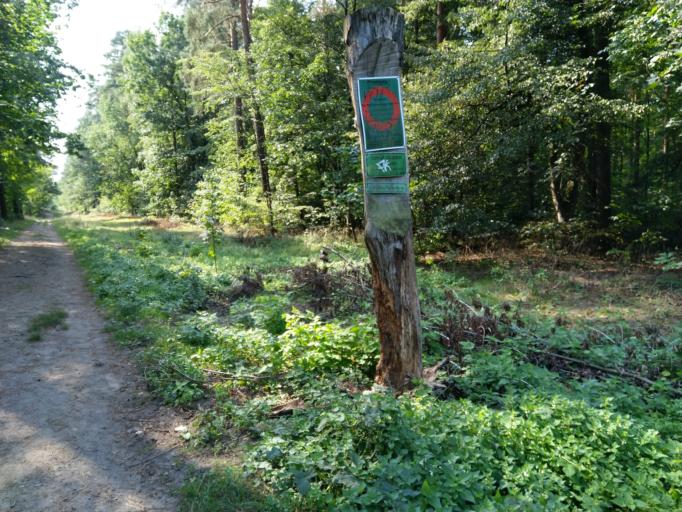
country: DE
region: Brandenburg
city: Woltersdorf
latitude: 52.4506
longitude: 13.7304
